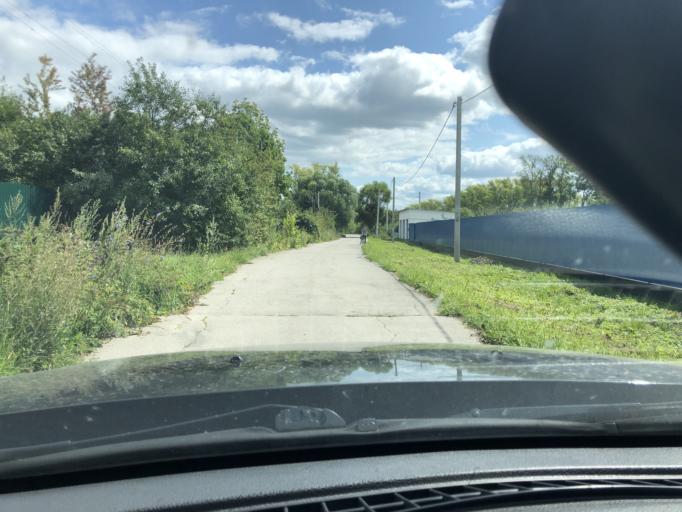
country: RU
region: Tula
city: Revyakino
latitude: 54.3481
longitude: 37.6168
